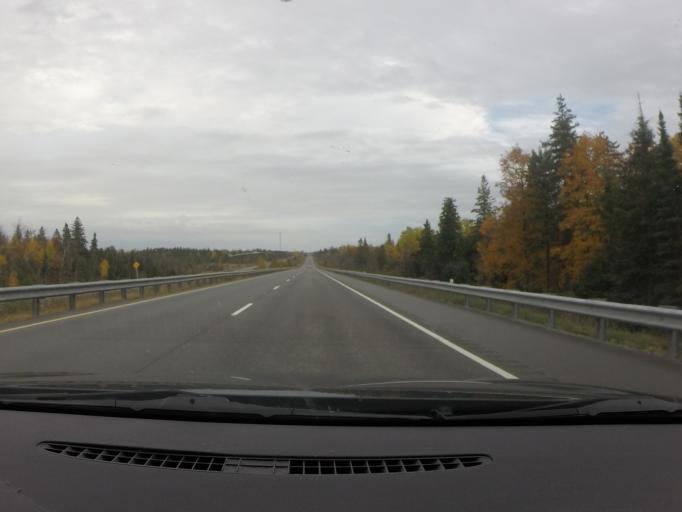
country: CA
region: Ontario
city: Carleton Place
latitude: 45.3258
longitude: -76.1259
